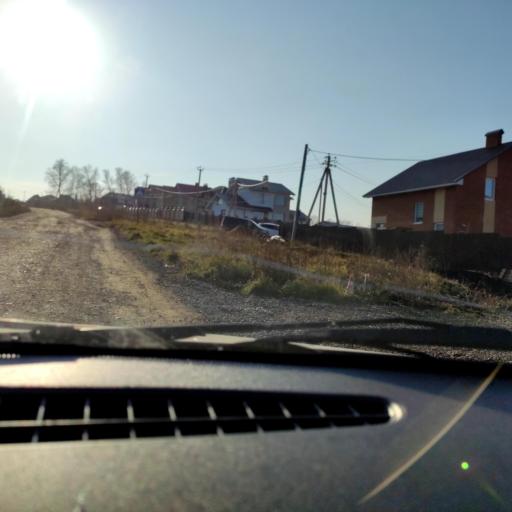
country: RU
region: Bashkortostan
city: Kabakovo
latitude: 54.6325
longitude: 56.0724
